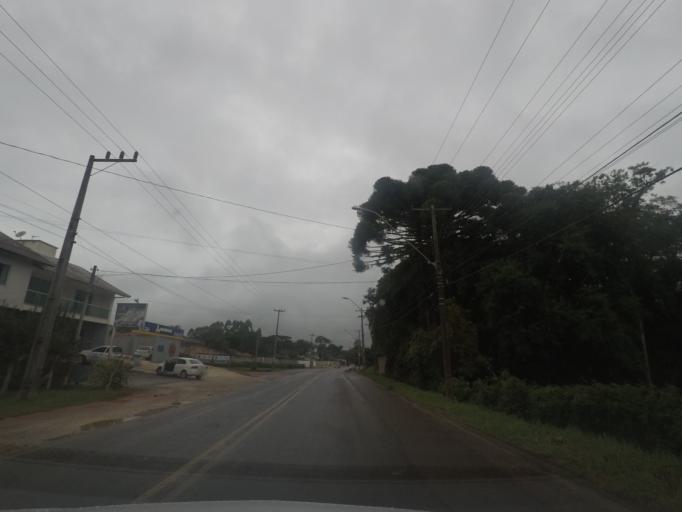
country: BR
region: Parana
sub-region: Quatro Barras
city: Quatro Barras
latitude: -25.3376
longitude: -49.0800
